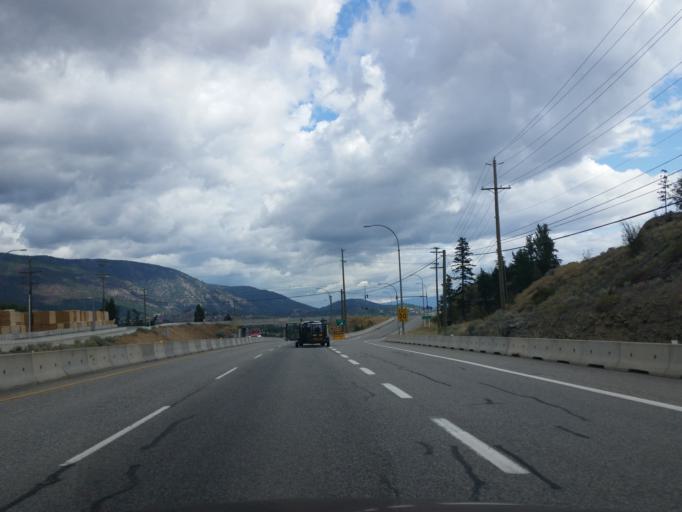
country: CA
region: British Columbia
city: West Kelowna
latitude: 49.8191
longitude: -119.6521
